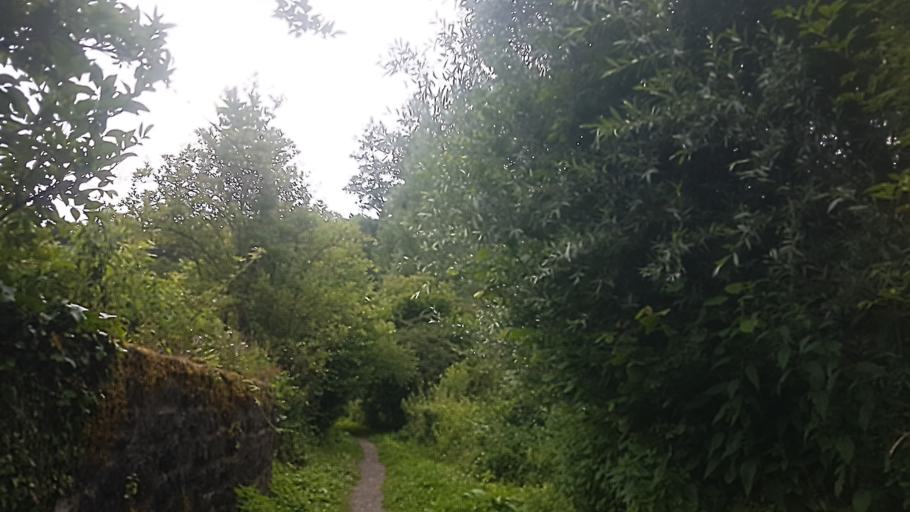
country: BE
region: Wallonia
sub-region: Province de Namur
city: Couvin
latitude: 50.0883
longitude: 4.5940
